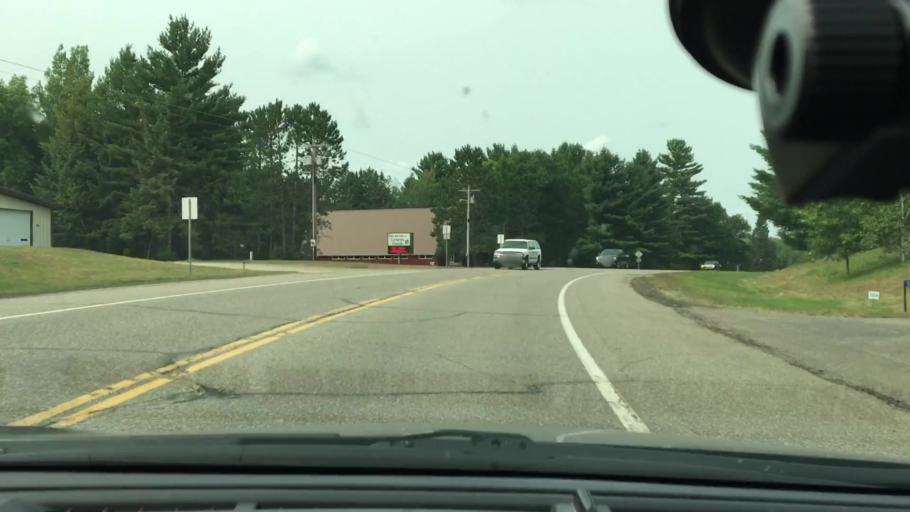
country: US
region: Minnesota
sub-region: Crow Wing County
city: Cross Lake
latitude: 46.8209
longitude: -93.9483
